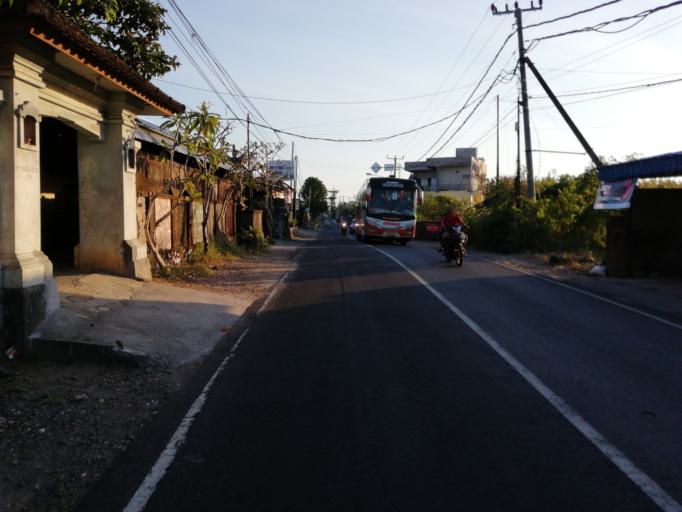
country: ID
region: Bali
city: Jimbaran
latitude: -8.8249
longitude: 115.1842
